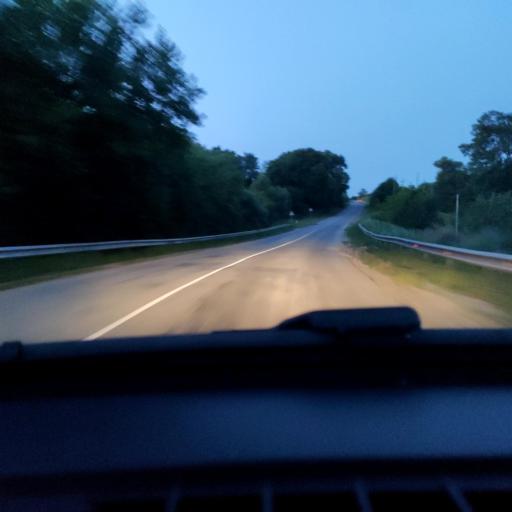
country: RU
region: Lipetsk
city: Zadonsk
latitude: 52.2919
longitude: 38.7621
